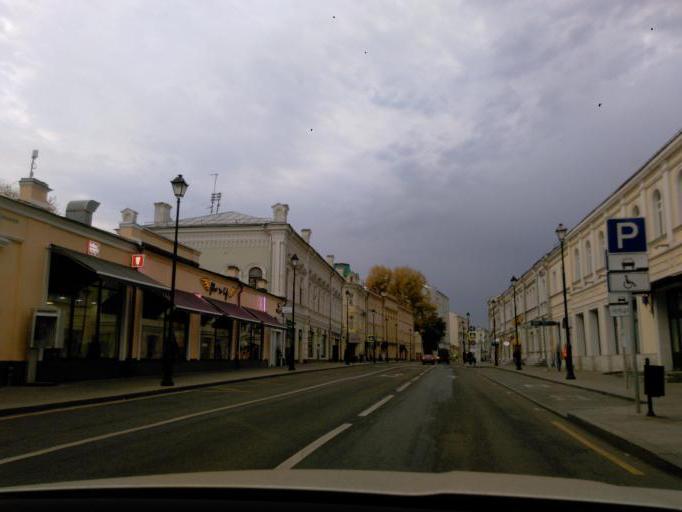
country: RU
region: Moscow
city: Moscow
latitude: 55.7582
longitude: 37.6386
